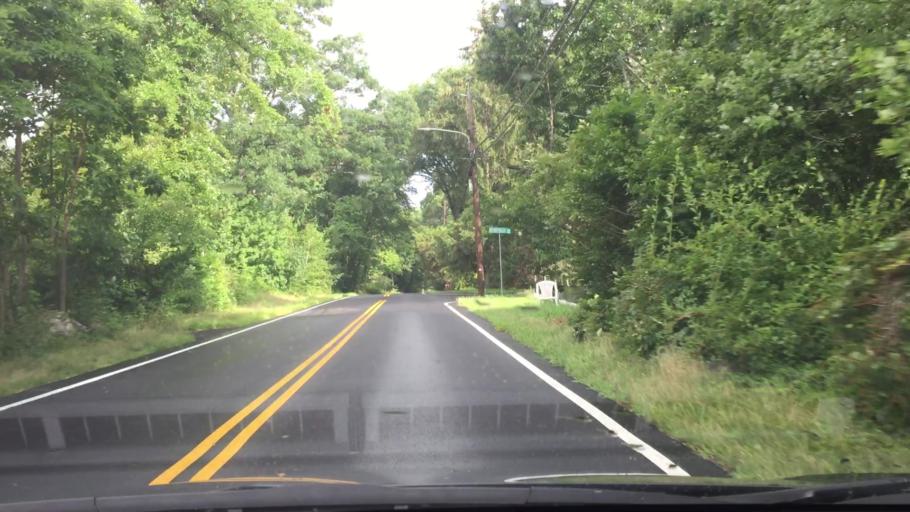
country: US
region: Massachusetts
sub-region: Middlesex County
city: Littleton Common
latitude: 42.5197
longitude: -71.4567
